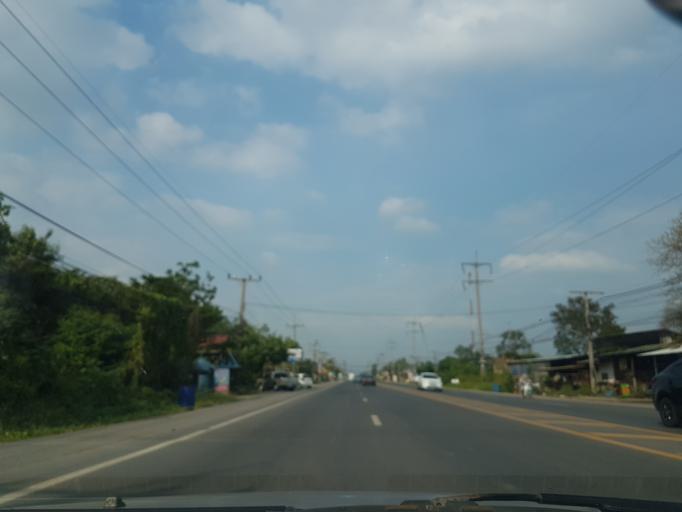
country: TH
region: Phra Nakhon Si Ayutthaya
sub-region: Amphoe Tha Ruea
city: Tha Ruea
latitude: 14.5823
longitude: 100.7295
